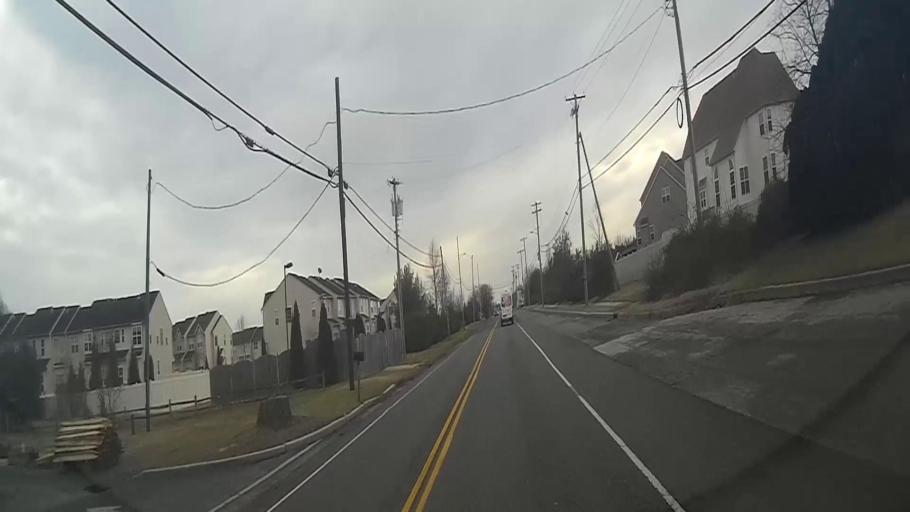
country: US
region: New Jersey
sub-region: Camden County
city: Berlin
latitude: 39.7892
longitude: -74.9429
